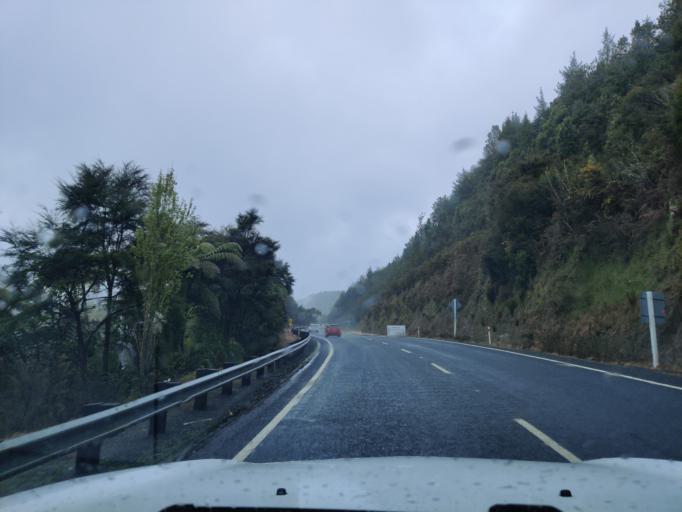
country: NZ
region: Waikato
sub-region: South Waikato District
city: Tokoroa
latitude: -38.0062
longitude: 175.9243
